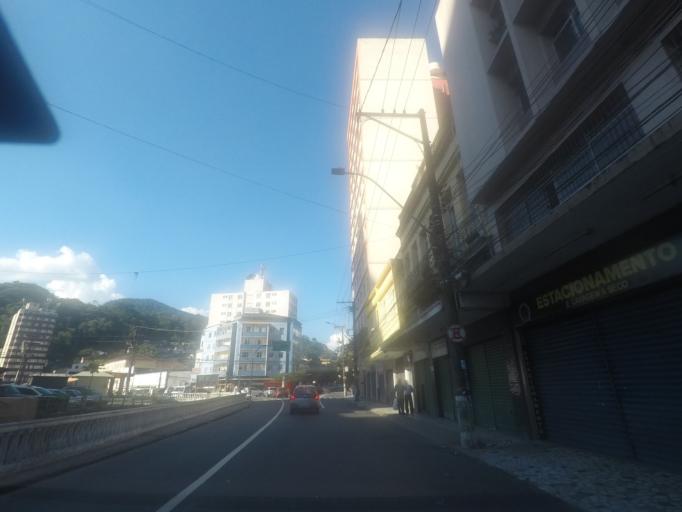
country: BR
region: Rio de Janeiro
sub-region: Petropolis
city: Petropolis
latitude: -22.5093
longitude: -43.1694
